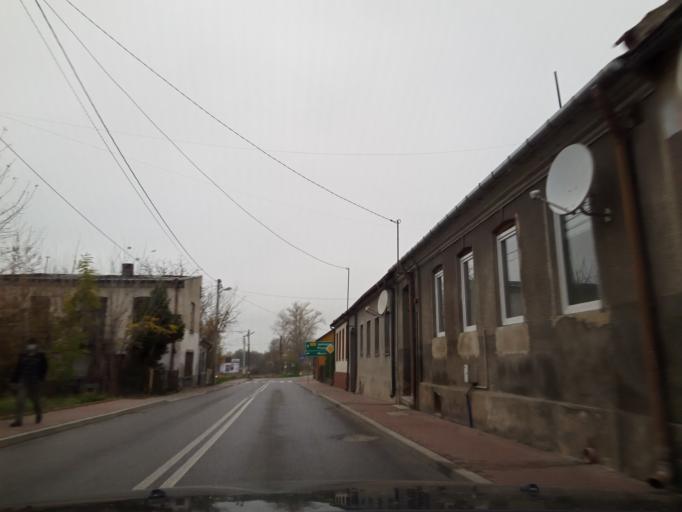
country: PL
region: Swietokrzyskie
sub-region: Powiat pinczowski
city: Dzialoszyce
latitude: 50.3668
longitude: 20.3486
